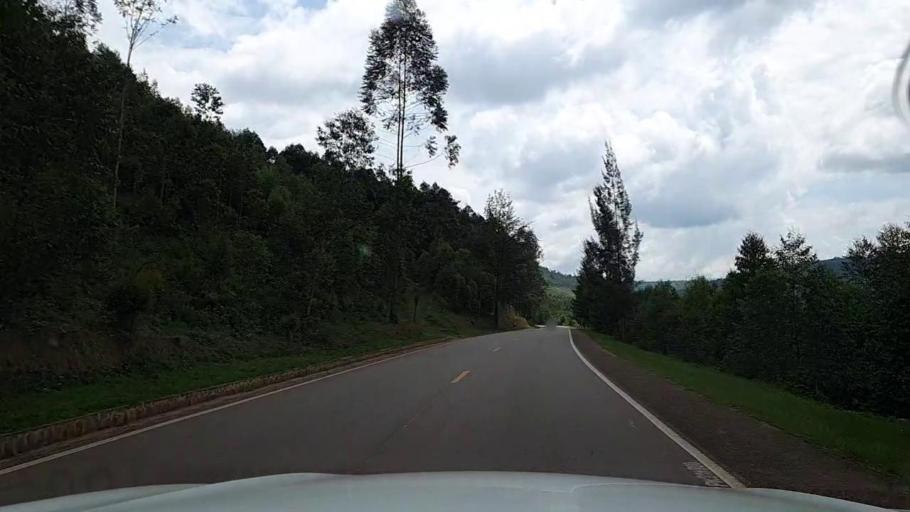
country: RW
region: Kigali
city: Kigali
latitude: -1.8116
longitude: 30.1004
